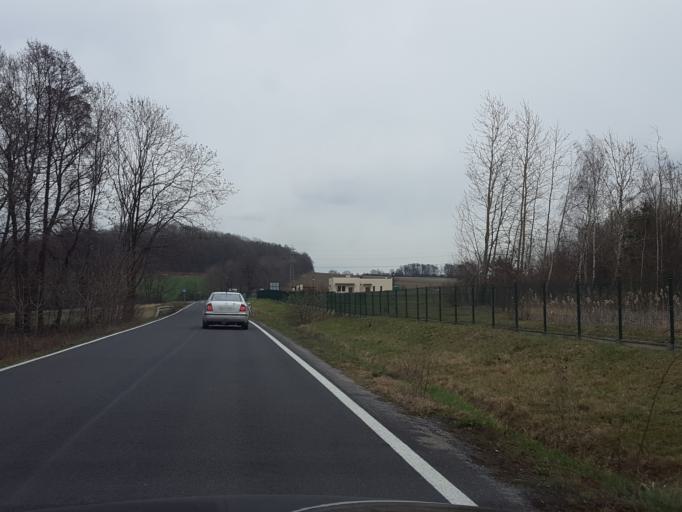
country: PL
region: Silesian Voivodeship
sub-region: Powiat mikolowski
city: Laziska Gorne
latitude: 50.1828
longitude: 18.8271
